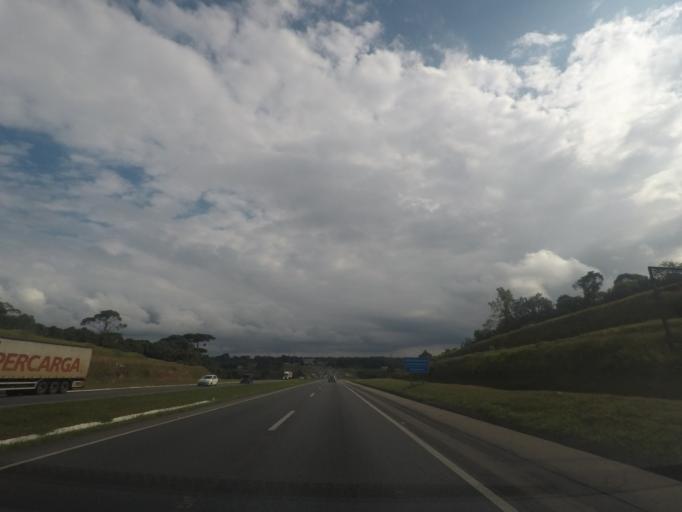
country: BR
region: Parana
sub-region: Piraquara
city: Piraquara
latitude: -25.4783
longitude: -49.0997
